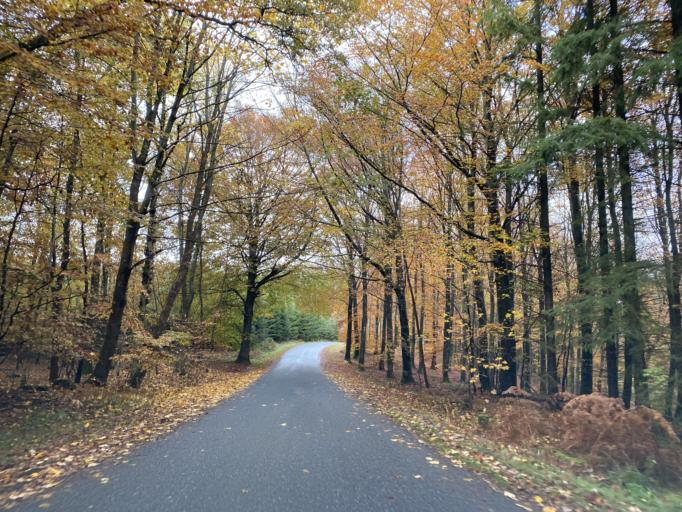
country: DK
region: Central Jutland
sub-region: Favrskov Kommune
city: Hammel
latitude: 56.2299
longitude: 9.9295
